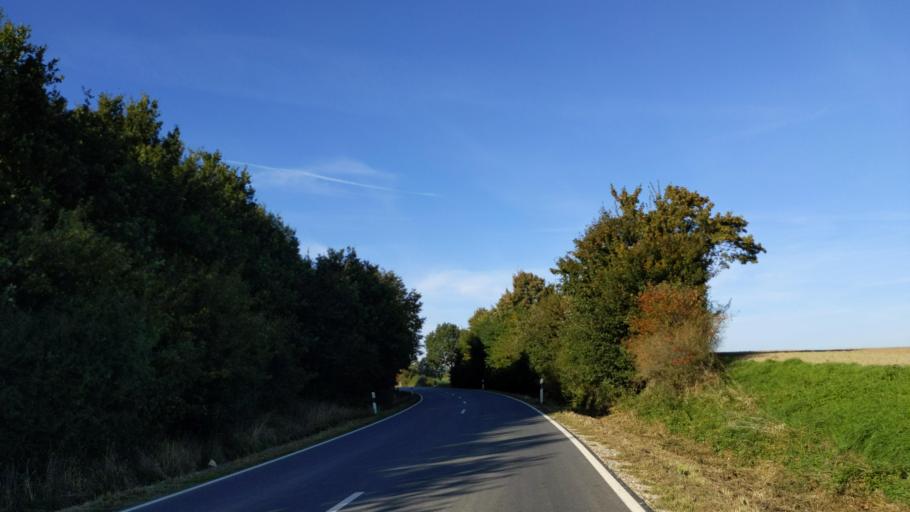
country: DE
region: Schleswig-Holstein
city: Eutin
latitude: 54.0744
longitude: 10.5919
